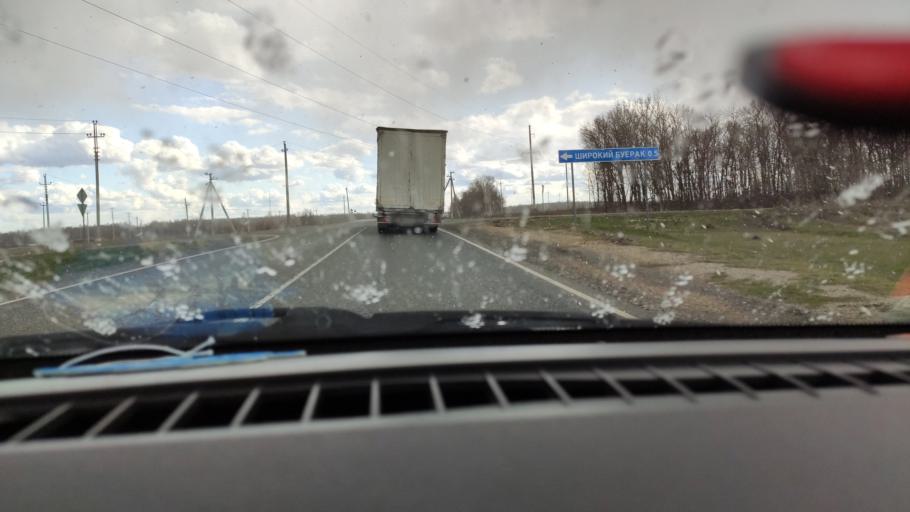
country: RU
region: Saratov
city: Balakovo
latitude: 52.1147
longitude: 47.7505
